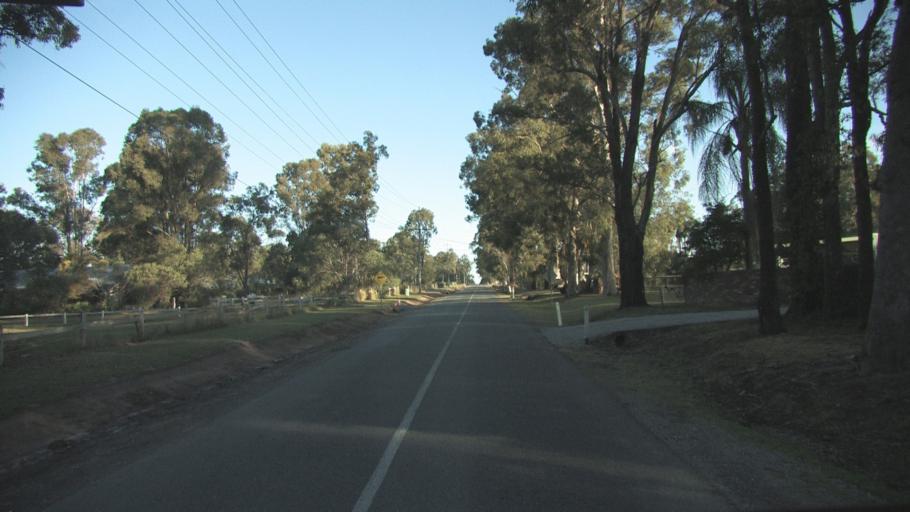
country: AU
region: Queensland
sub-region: Logan
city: Waterford West
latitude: -27.7199
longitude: 153.1484
